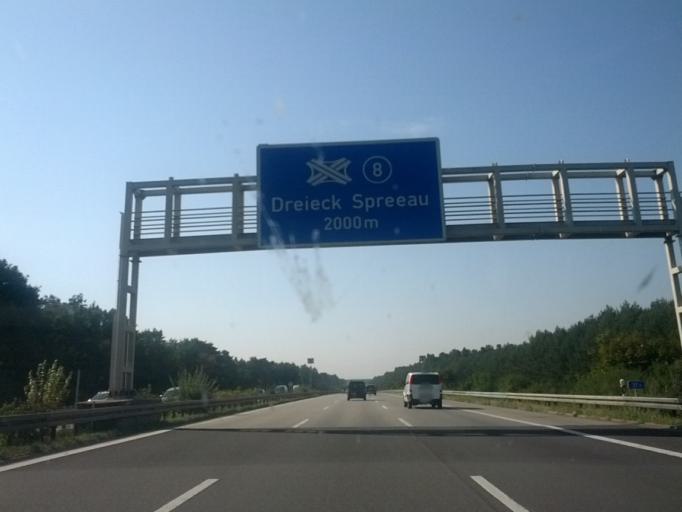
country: DE
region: Brandenburg
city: Erkner
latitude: 52.3498
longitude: 13.7571
